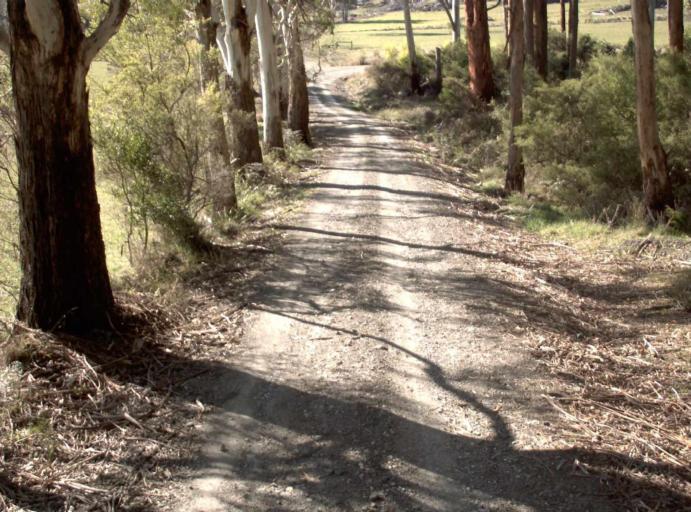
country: AU
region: Tasmania
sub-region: Launceston
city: Mayfield
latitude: -41.2498
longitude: 147.1833
